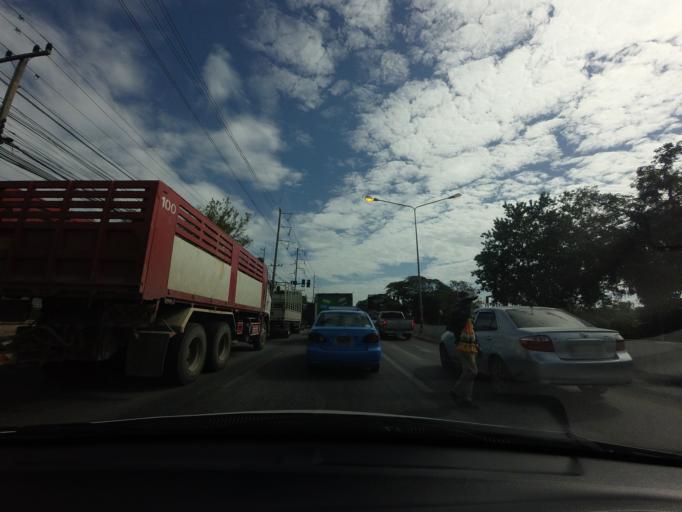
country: TH
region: Pathum Thani
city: Nong Suea
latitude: 14.0574
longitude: 100.8372
